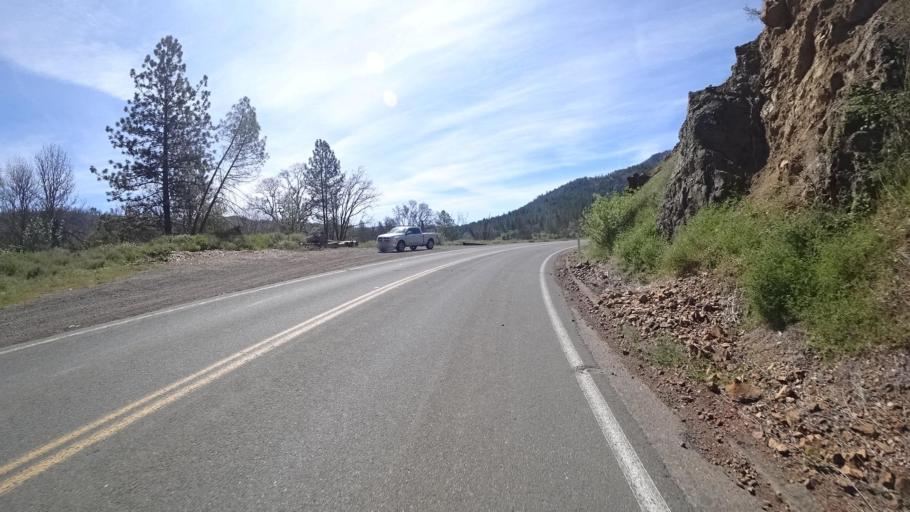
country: US
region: California
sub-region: Lake County
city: Cobb
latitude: 38.8408
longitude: -122.7473
